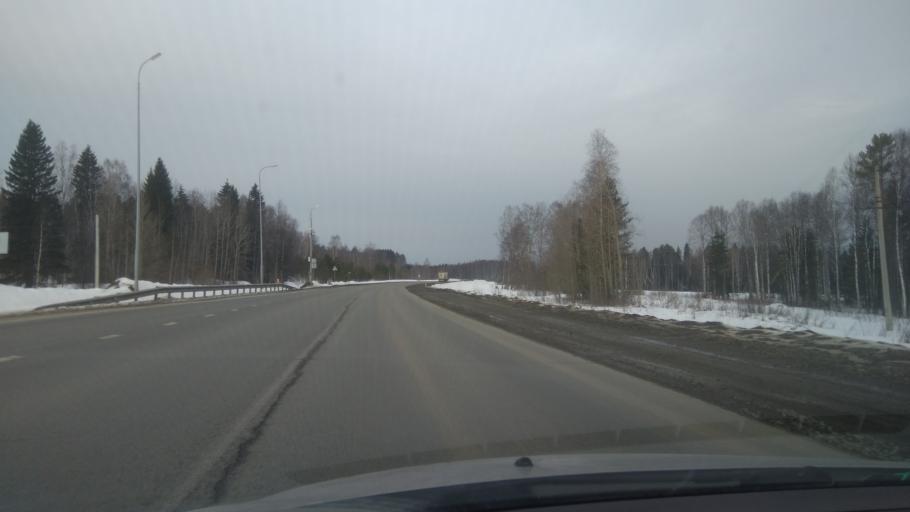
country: RU
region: Sverdlovsk
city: Ufimskiy
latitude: 56.7822
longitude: 58.4001
